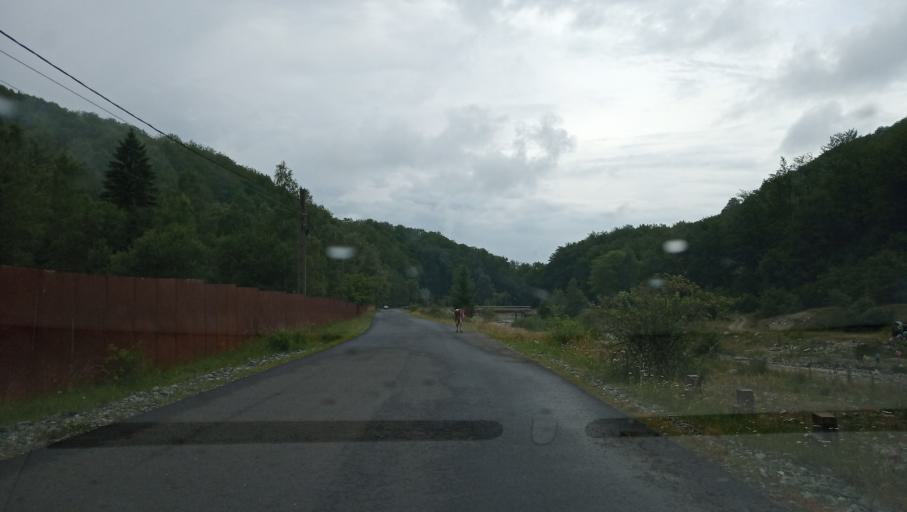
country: RO
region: Hunedoara
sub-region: Oras Petrila
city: Petrila
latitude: 45.4167
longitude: 23.4518
